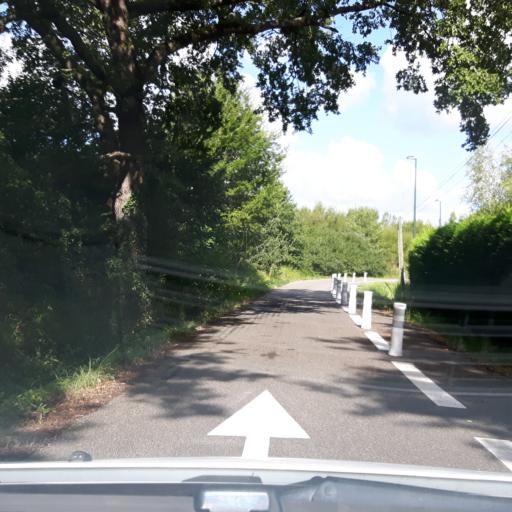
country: FR
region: Midi-Pyrenees
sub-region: Departement de la Haute-Garonne
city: Bouloc
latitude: 43.7899
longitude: 1.4089
